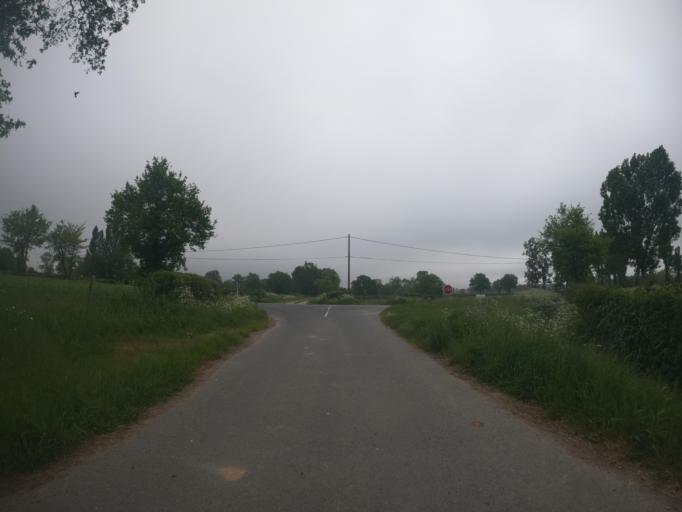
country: FR
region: Poitou-Charentes
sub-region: Departement des Deux-Sevres
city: Chiche
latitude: 46.8821
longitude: -0.3271
